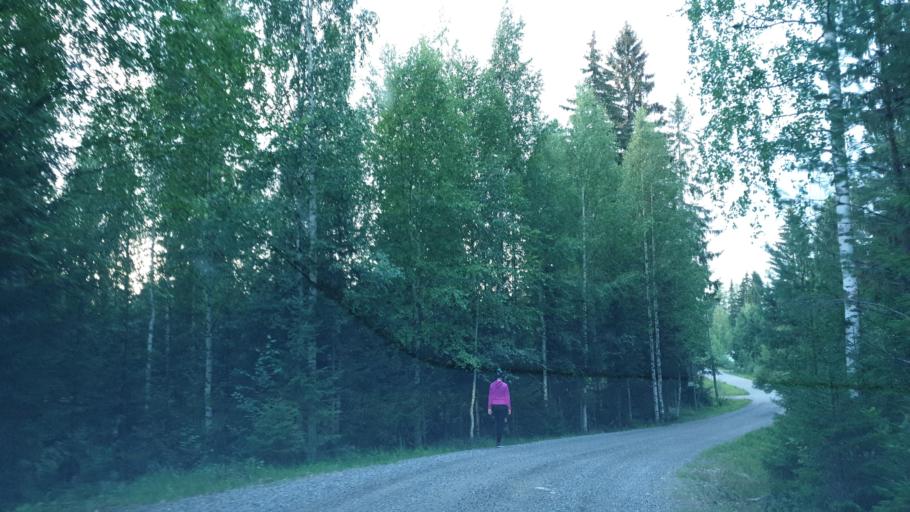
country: FI
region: Northern Savo
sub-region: Varkaus
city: Leppaevirta
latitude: 62.5816
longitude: 27.6237
